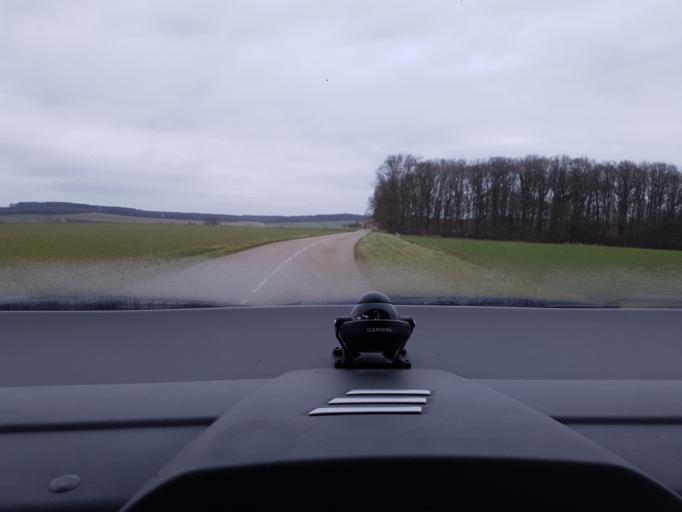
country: FR
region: Lorraine
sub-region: Departement de la Moselle
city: Dieuze
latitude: 48.7623
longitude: 6.6940
